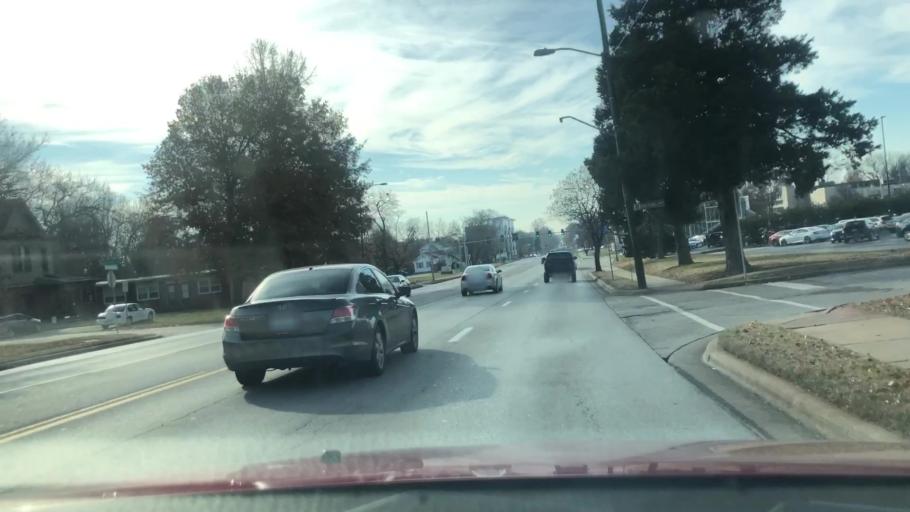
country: US
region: Missouri
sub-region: Greene County
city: Springfield
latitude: 37.2028
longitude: -93.2762
